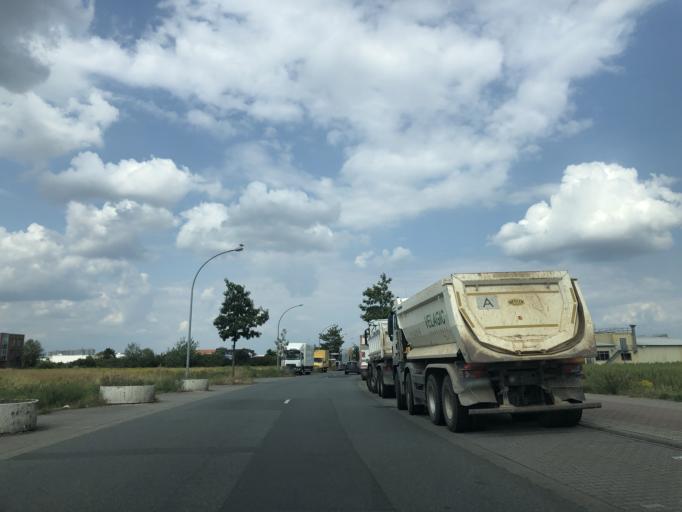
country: DE
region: Hesse
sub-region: Regierungsbezirk Darmstadt
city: Dietzenbach
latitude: 50.0105
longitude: 8.7920
